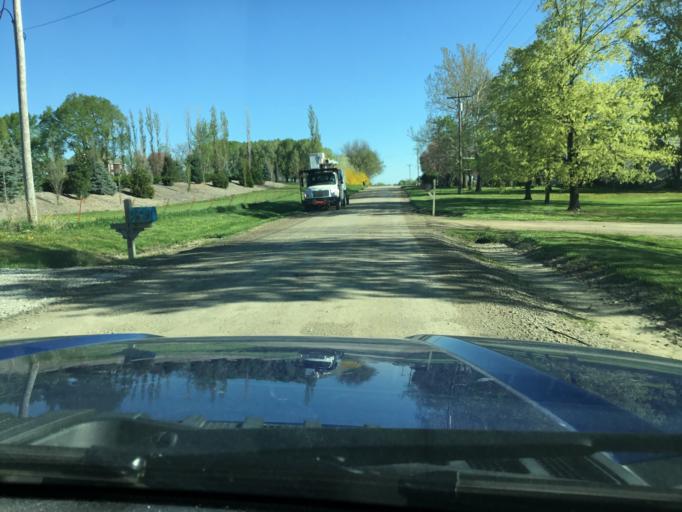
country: US
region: Kansas
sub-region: Douglas County
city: Lawrence
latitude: 38.9785
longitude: -95.3539
